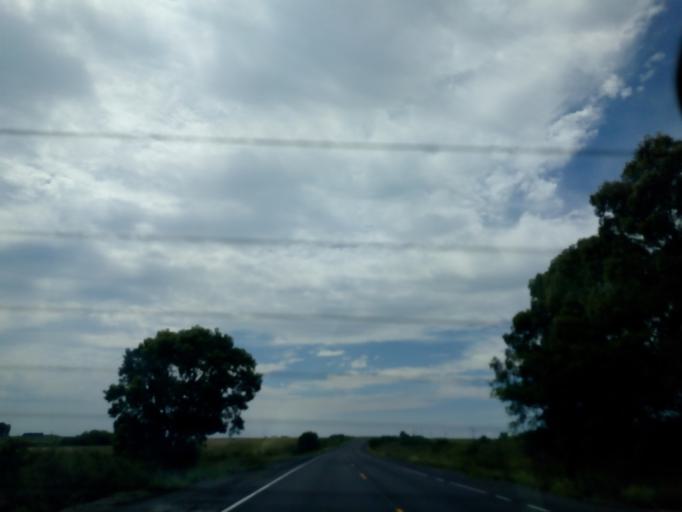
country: BR
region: Rio Grande do Sul
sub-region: Quarai
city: Quarai
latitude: -29.9726
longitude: -56.5565
